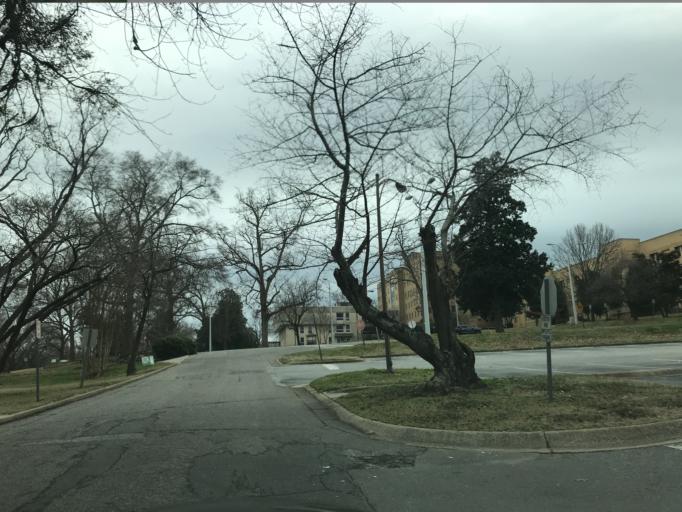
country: US
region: North Carolina
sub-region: Wake County
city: Raleigh
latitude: 35.7710
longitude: -78.6556
